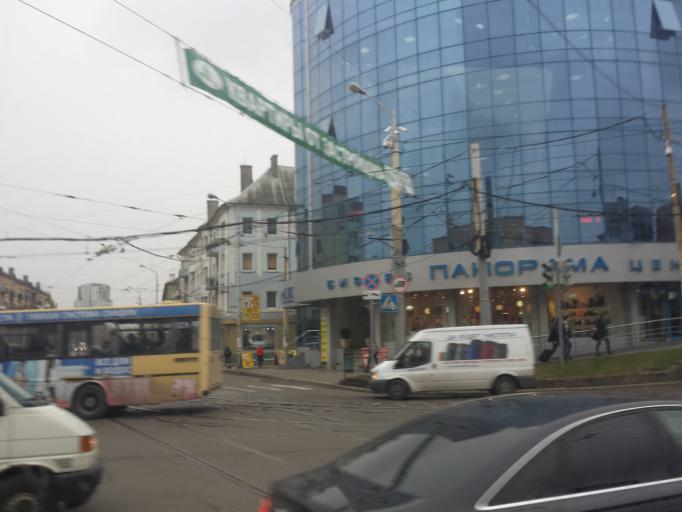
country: RU
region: Kaliningrad
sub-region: Gorod Kaliningrad
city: Kaliningrad
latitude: 54.6989
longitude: 20.5030
